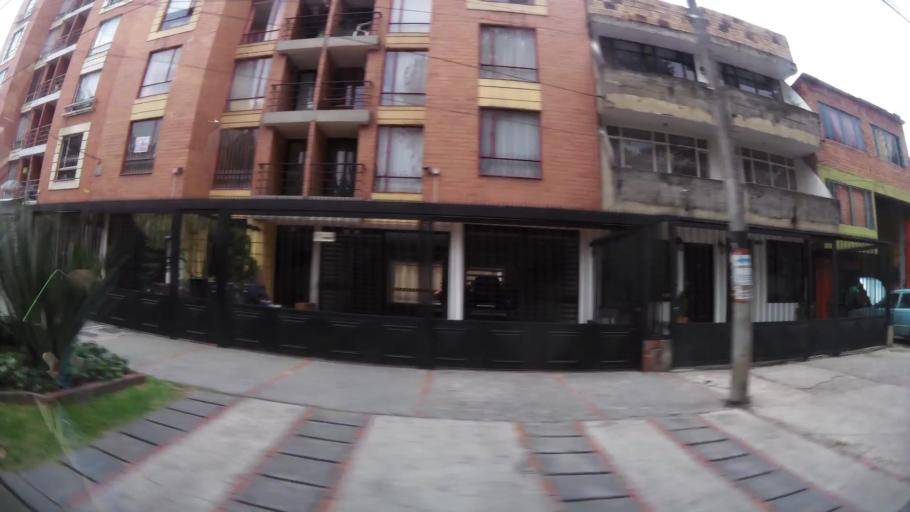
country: CO
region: Bogota D.C.
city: Bogota
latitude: 4.5929
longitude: -74.1016
